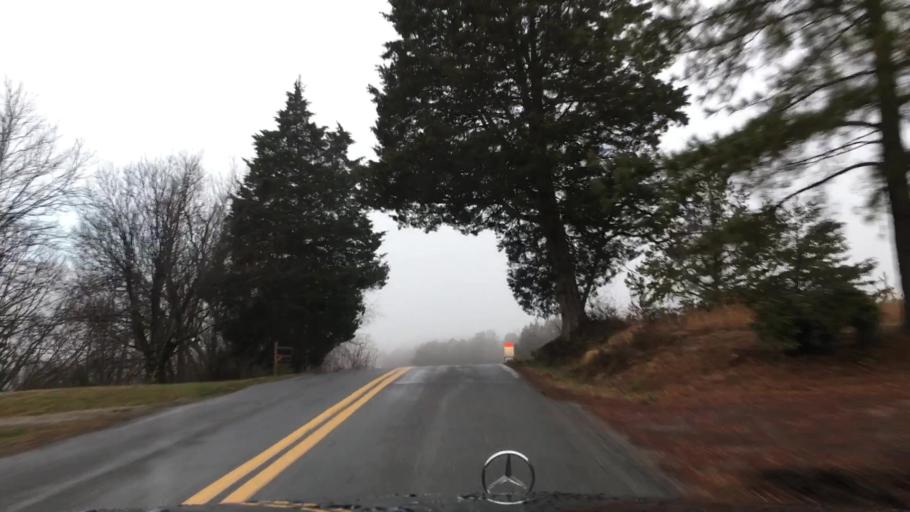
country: US
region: Virginia
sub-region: Pittsylvania County
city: Hurt
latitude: 37.1142
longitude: -79.3235
